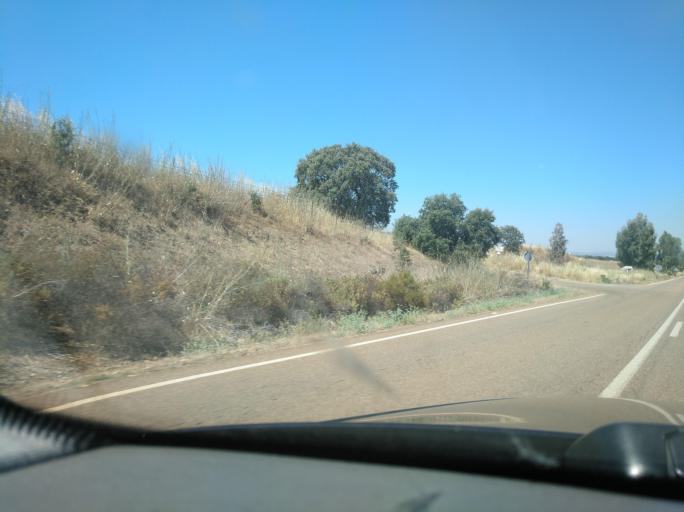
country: ES
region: Extremadura
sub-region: Provincia de Badajoz
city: Olivenza
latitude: 38.6999
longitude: -7.1487
